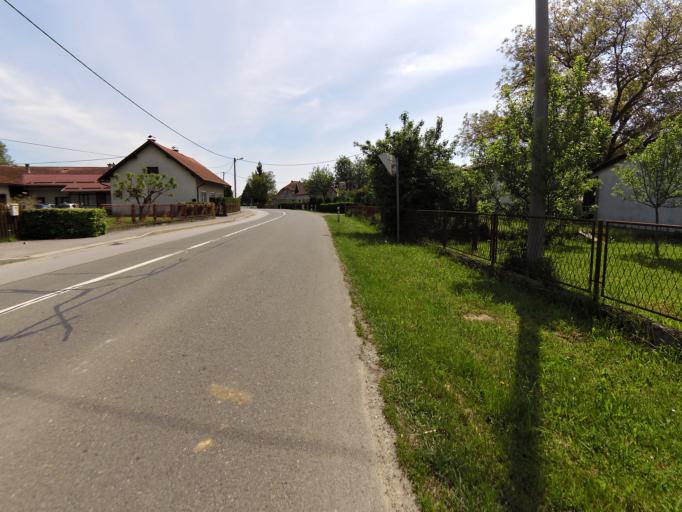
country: HR
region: Karlovacka
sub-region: Grad Karlovac
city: Karlovac
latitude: 45.5414
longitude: 15.5375
